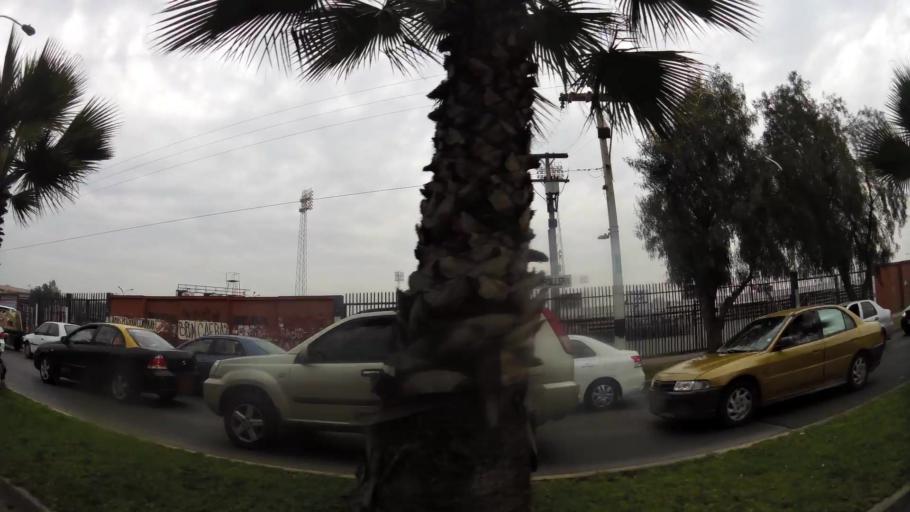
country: CL
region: Santiago Metropolitan
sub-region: Provincia de Santiago
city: Villa Presidente Frei, Nunoa, Santiago, Chile
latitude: -33.5072
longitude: -70.6040
